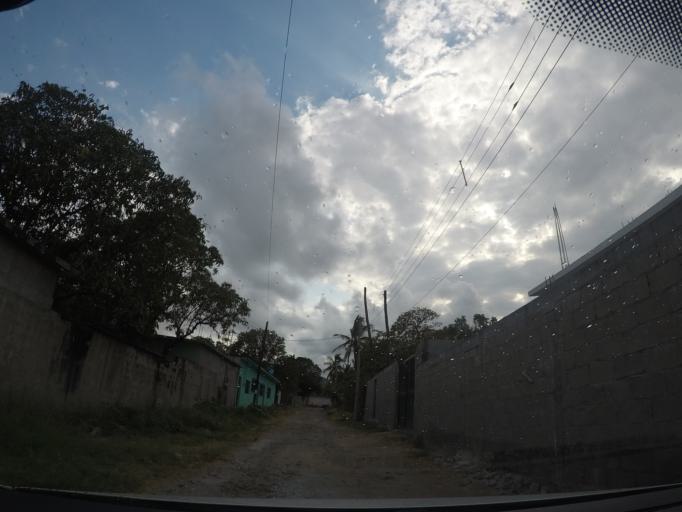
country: MX
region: Oaxaca
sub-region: Salina Cruz
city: Salina Cruz
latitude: 16.2093
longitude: -95.2059
